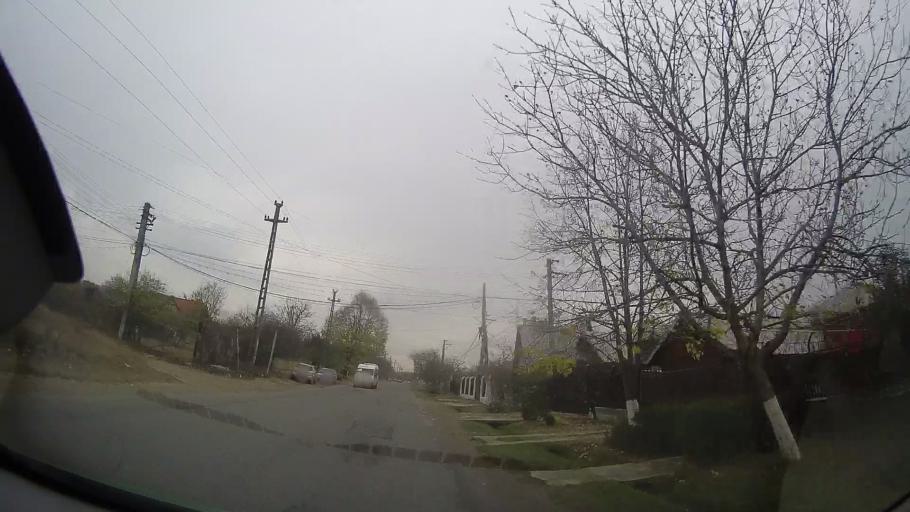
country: RO
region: Prahova
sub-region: Oras Urlati
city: Urlati
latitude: 45.0021
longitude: 26.2273
